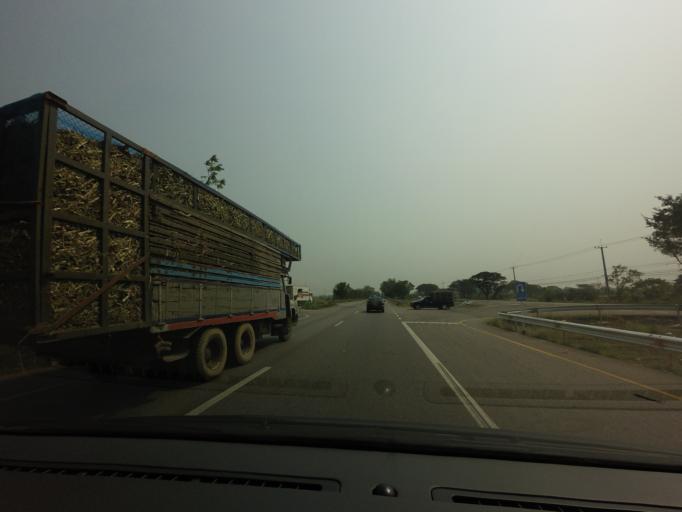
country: TH
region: Prachuap Khiri Khan
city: Pran Buri
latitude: 12.4480
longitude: 99.9055
